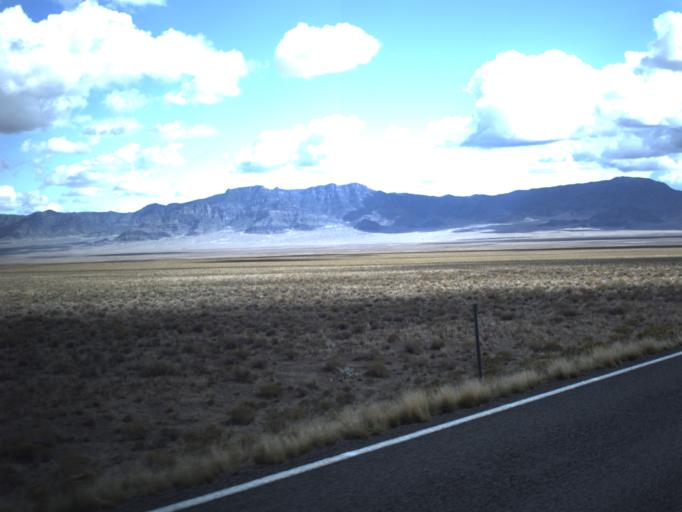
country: US
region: Utah
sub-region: Beaver County
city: Milford
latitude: 38.5638
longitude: -113.7673
